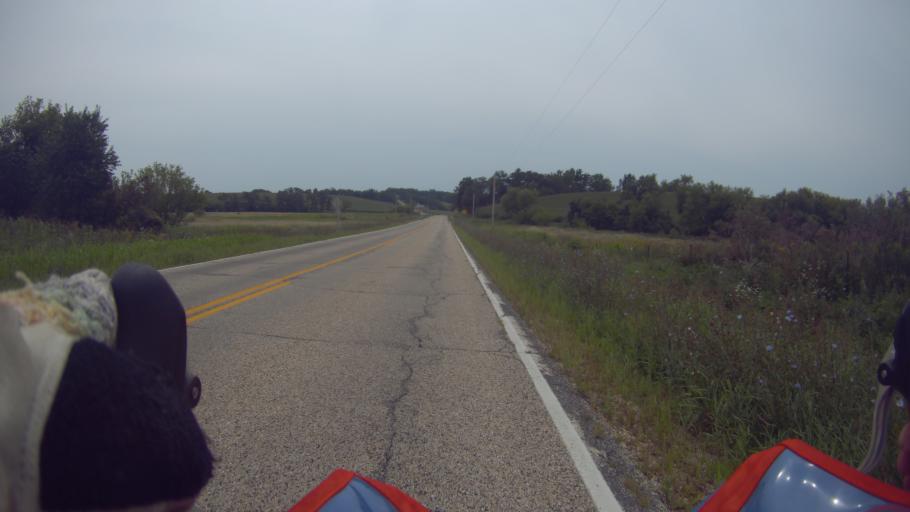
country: US
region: Wisconsin
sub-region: Dane County
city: Mount Horeb
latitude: 42.9342
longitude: -89.6756
